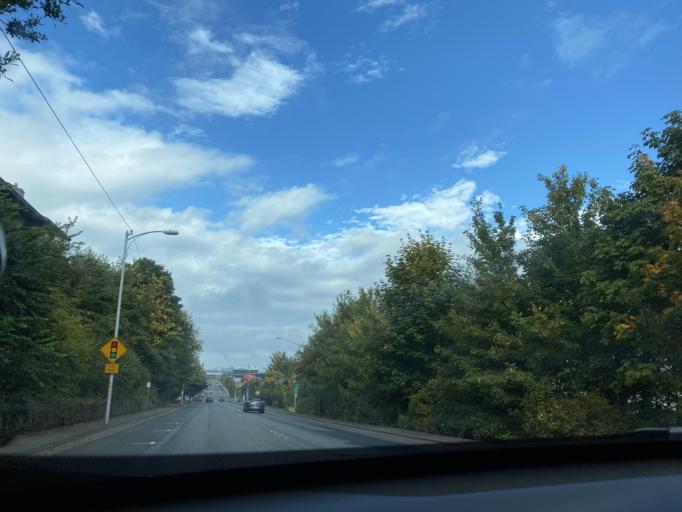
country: US
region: Washington
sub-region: Clallam County
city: Port Angeles
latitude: 48.1180
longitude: -123.4281
